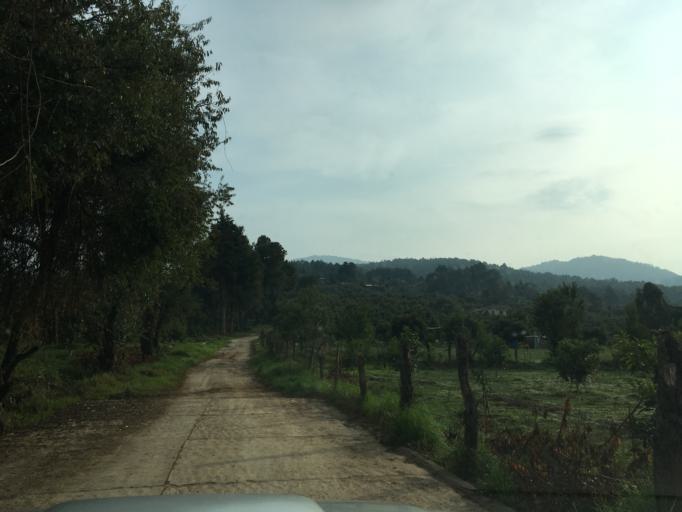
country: MX
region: Michoacan
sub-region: Zitacuaro
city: La Fundicion (Quinta Manzana)
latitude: 19.4859
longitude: -100.3137
